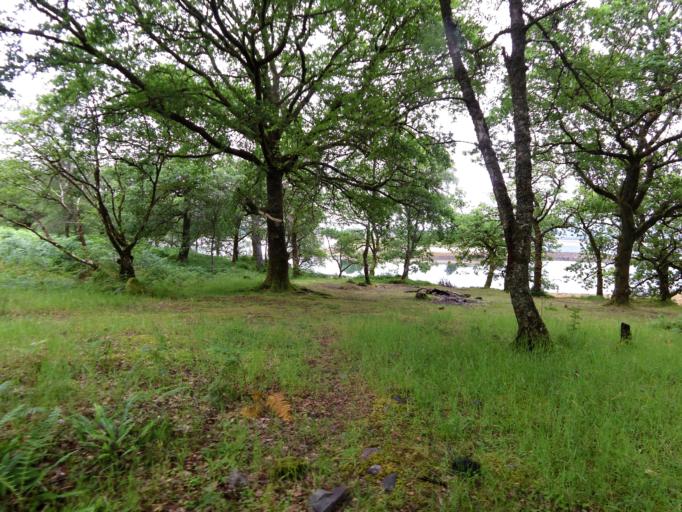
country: GB
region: Scotland
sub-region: Highland
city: Fort William
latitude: 56.8333
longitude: -5.1244
